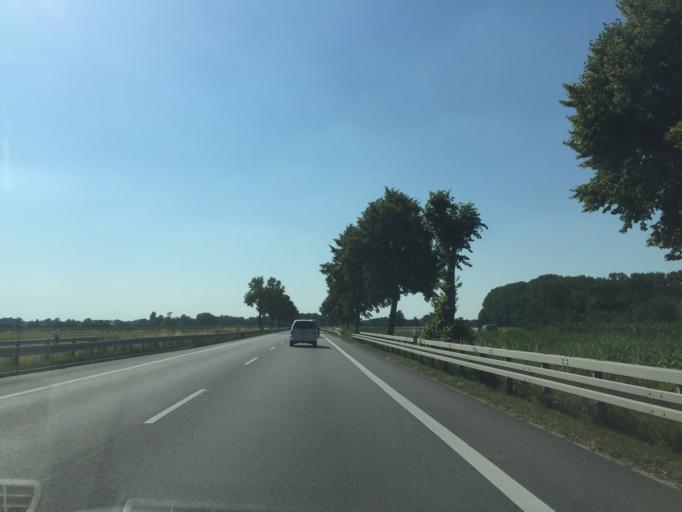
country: DE
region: Hesse
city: Lorsch
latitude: 49.6505
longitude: 8.5944
